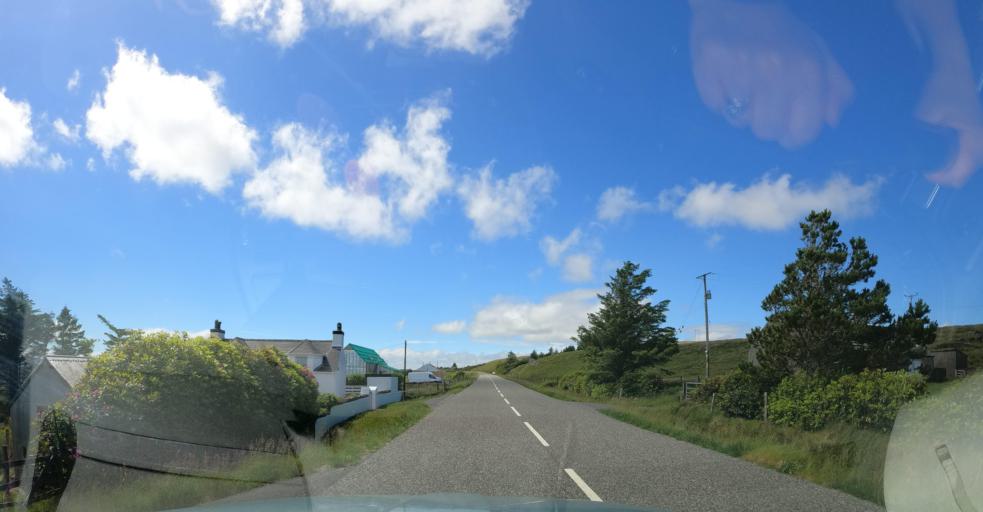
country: GB
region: Scotland
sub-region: Eilean Siar
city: Stornoway
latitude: 58.1650
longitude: -6.5502
